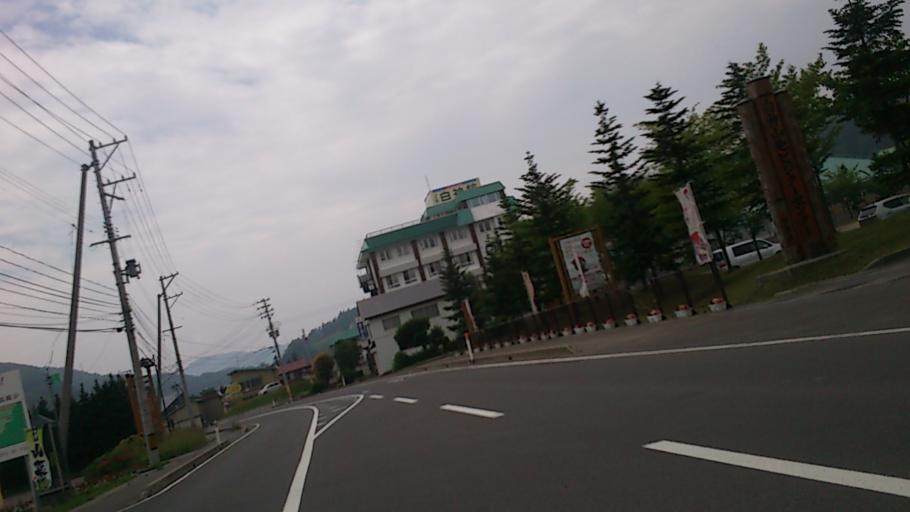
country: JP
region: Aomori
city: Hirosaki
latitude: 40.5784
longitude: 140.3000
